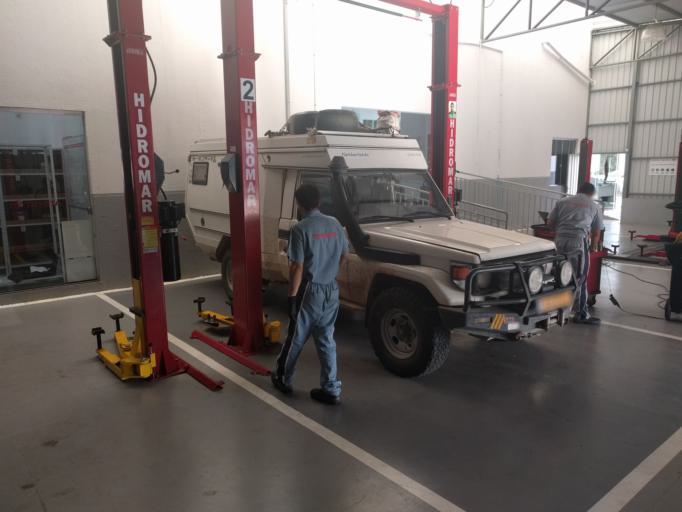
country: BR
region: Parana
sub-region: Foz Do Iguacu
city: Foz do Iguacu
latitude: -25.5223
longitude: -54.5623
